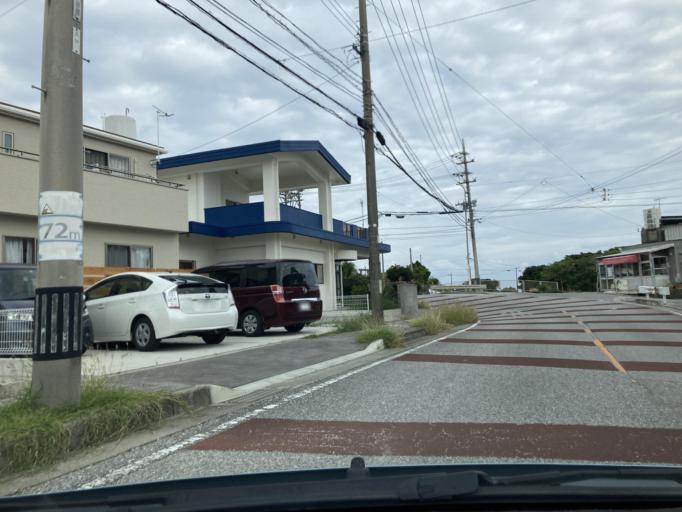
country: JP
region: Okinawa
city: Tomigusuku
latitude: 26.1414
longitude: 127.7918
